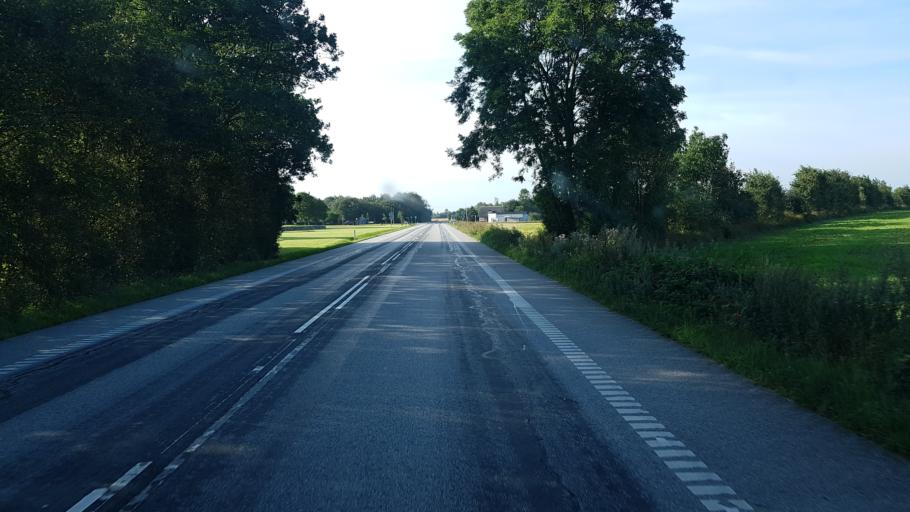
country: DK
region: South Denmark
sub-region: Haderslev Kommune
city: Vojens
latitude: 55.2806
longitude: 9.2890
